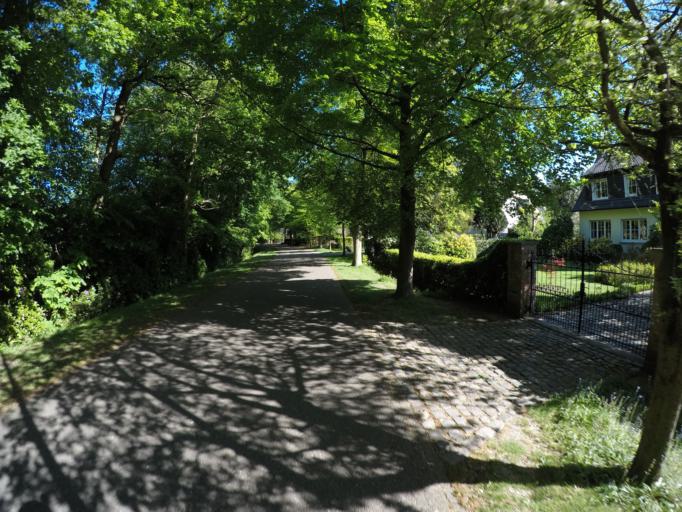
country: BE
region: Flanders
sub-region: Provincie Antwerpen
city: Schoten
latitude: 51.2509
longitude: 4.5207
